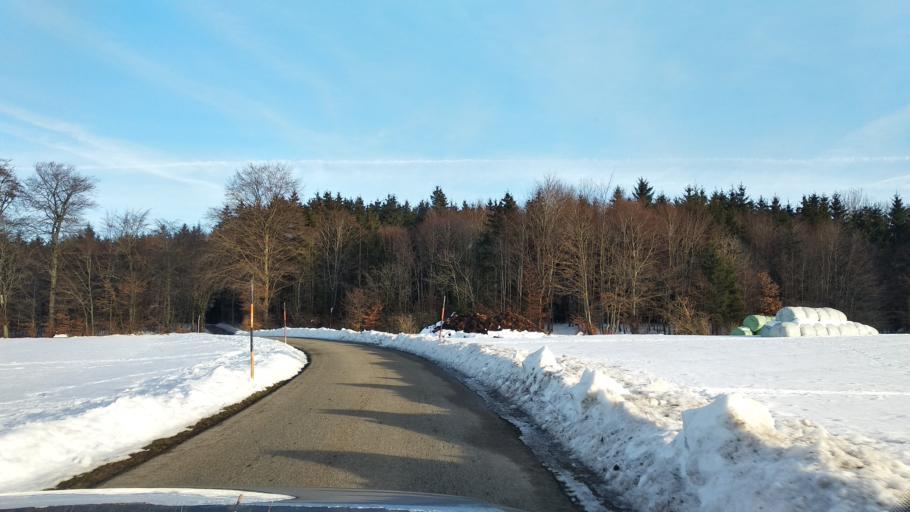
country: DE
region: Bavaria
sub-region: Upper Bavaria
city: Kirchseeon
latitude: 48.0691
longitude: 11.8736
